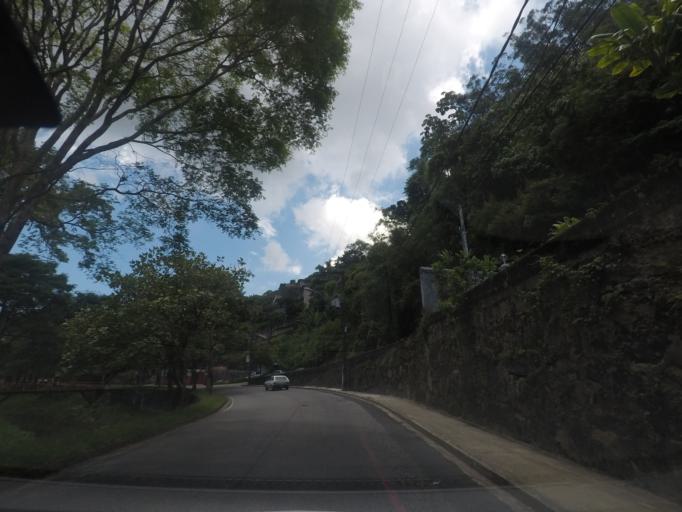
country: BR
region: Rio de Janeiro
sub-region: Petropolis
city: Petropolis
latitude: -22.4973
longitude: -43.1807
